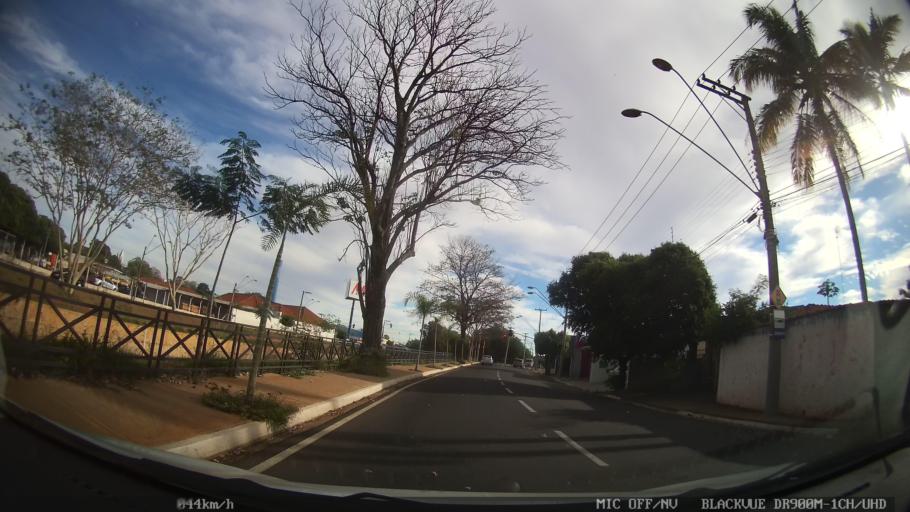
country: BR
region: Sao Paulo
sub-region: Catanduva
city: Catanduva
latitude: -21.1293
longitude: -48.9792
